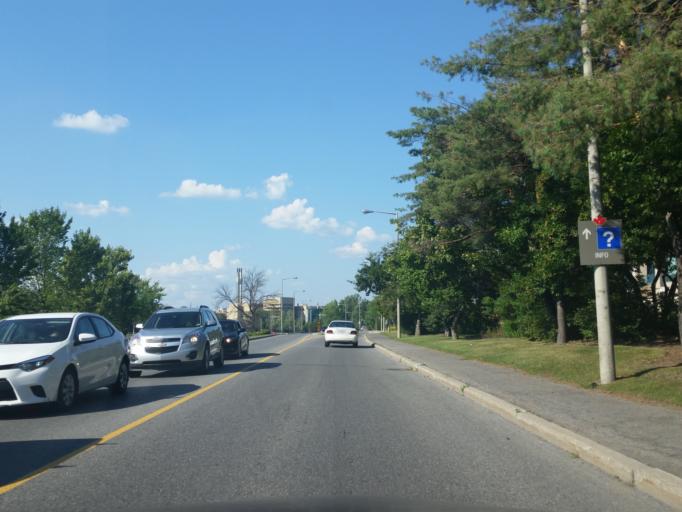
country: CA
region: Ontario
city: Ottawa
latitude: 45.4141
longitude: -75.6822
